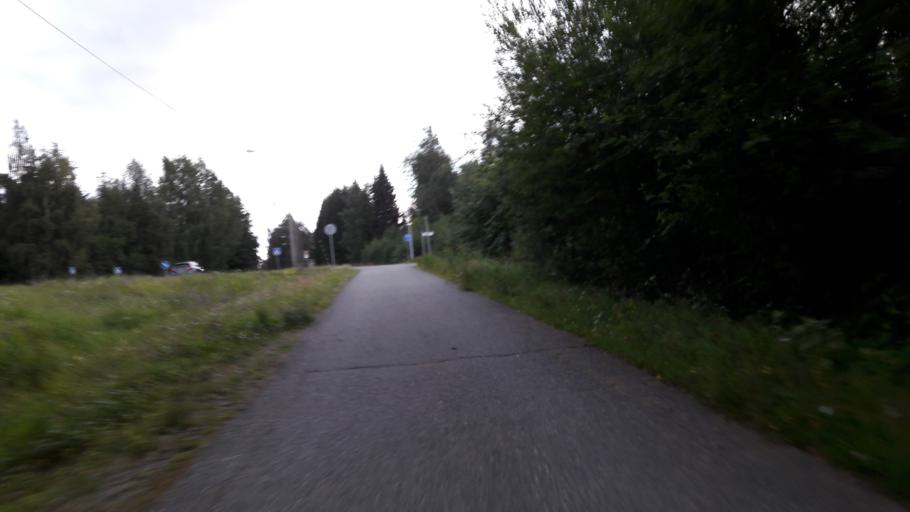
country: FI
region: North Karelia
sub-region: Joensuu
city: Joensuu
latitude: 62.5482
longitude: 29.8283
